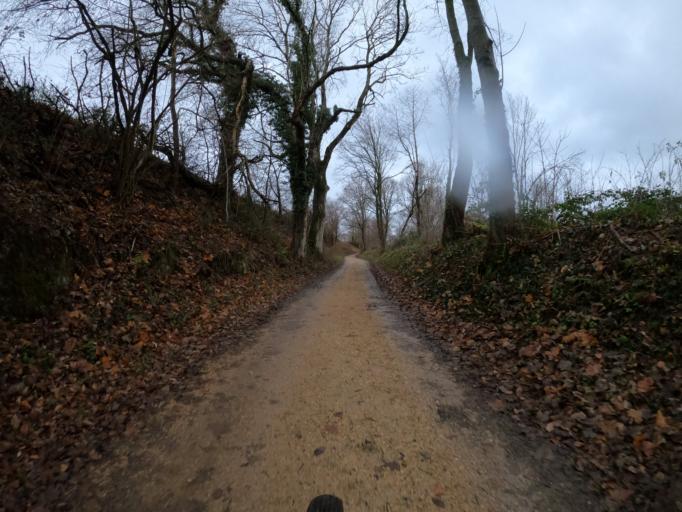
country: DE
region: Baden-Wuerttemberg
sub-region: Regierungsbezirk Stuttgart
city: Sussen
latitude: 48.6948
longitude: 9.7667
